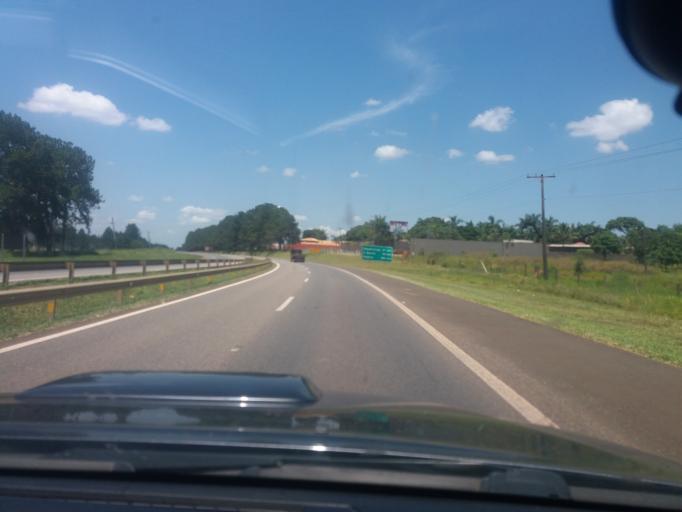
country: BR
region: Sao Paulo
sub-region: Tatui
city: Tatui
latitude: -23.3610
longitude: -47.8964
